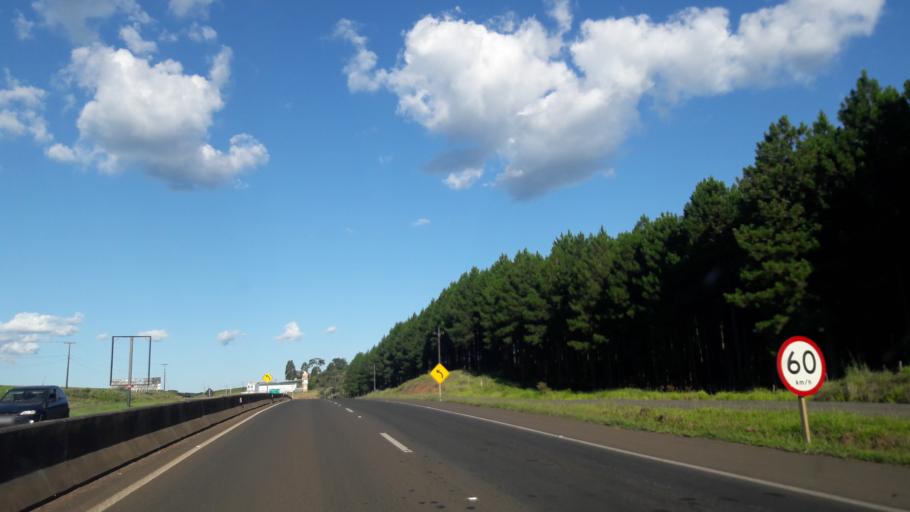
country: BR
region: Parana
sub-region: Guarapuava
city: Guarapuava
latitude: -25.3434
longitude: -51.4375
